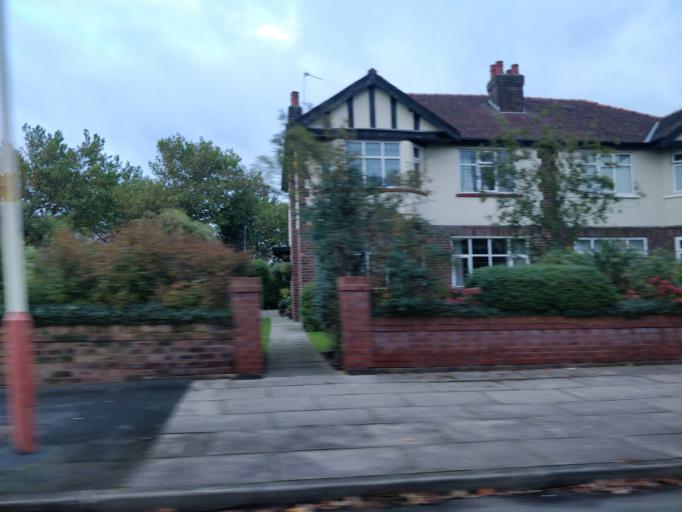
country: GB
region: England
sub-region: Sefton
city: Southport
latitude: 53.6634
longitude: -2.9722
